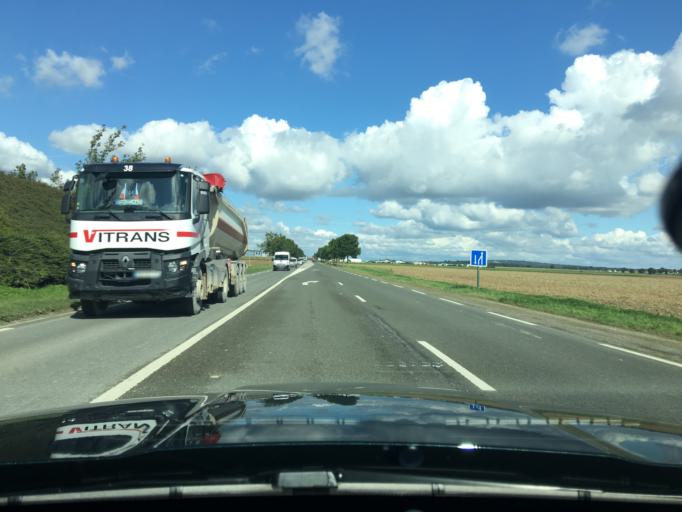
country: FR
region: Ile-de-France
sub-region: Departement du Val-d'Oise
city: Louvres
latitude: 49.0507
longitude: 2.5136
